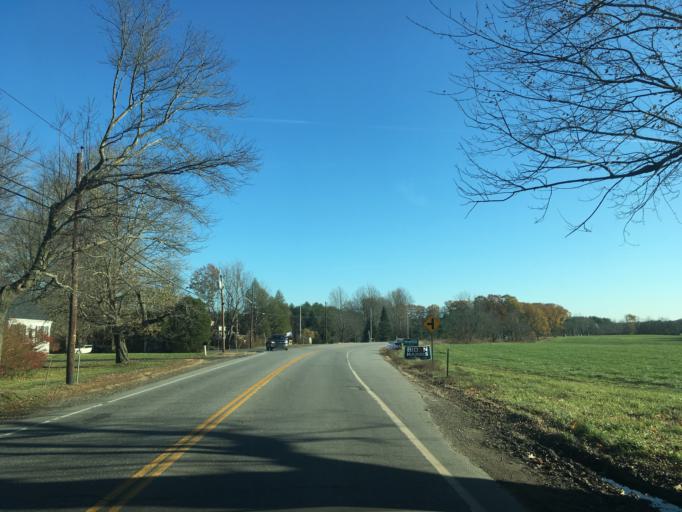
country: US
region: New Hampshire
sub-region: Rockingham County
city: Stratham Station
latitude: 43.0374
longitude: -70.9242
